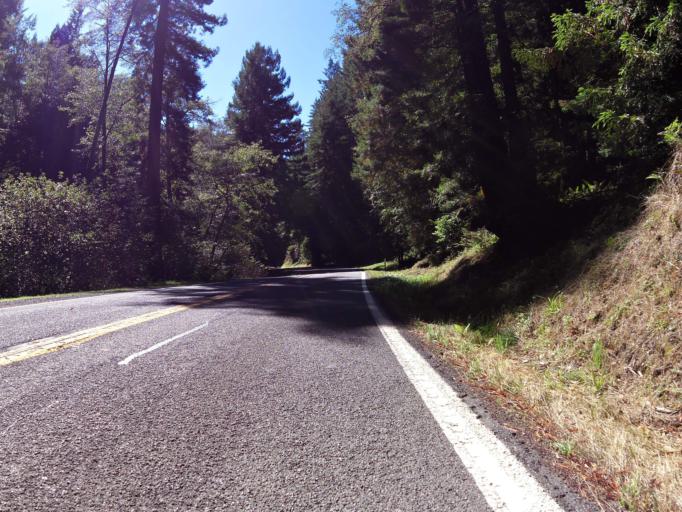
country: US
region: California
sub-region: Humboldt County
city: Redway
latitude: 39.7851
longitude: -123.8196
